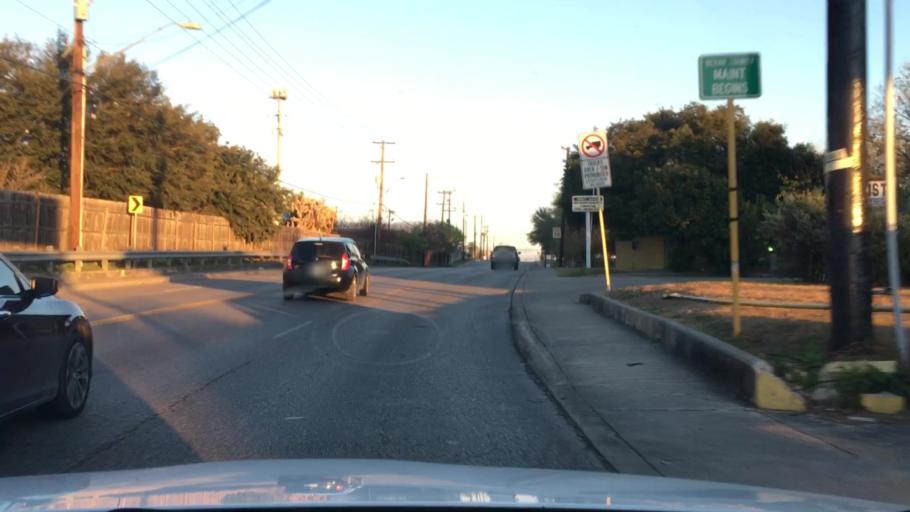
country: US
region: Texas
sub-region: Bexar County
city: Windcrest
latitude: 29.5120
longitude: -98.3661
